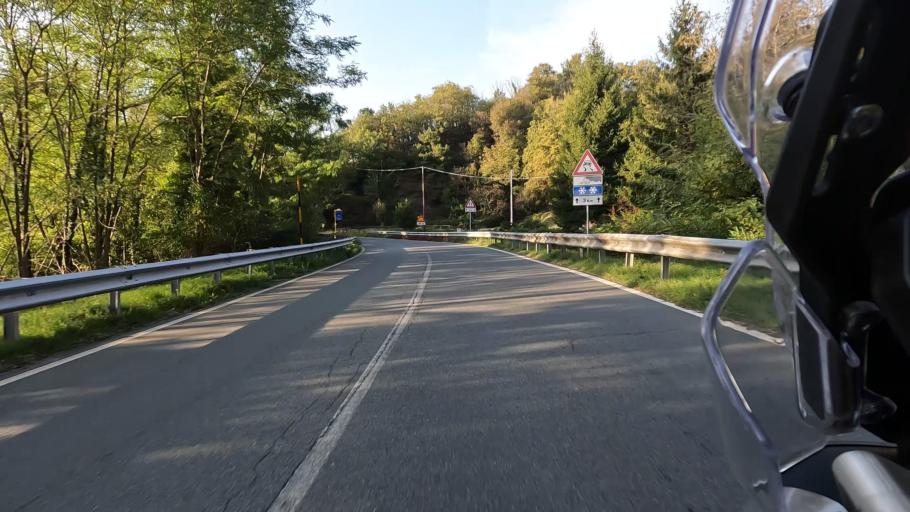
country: IT
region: Liguria
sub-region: Provincia di Savona
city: San Giovanni
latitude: 44.4062
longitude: 8.4904
